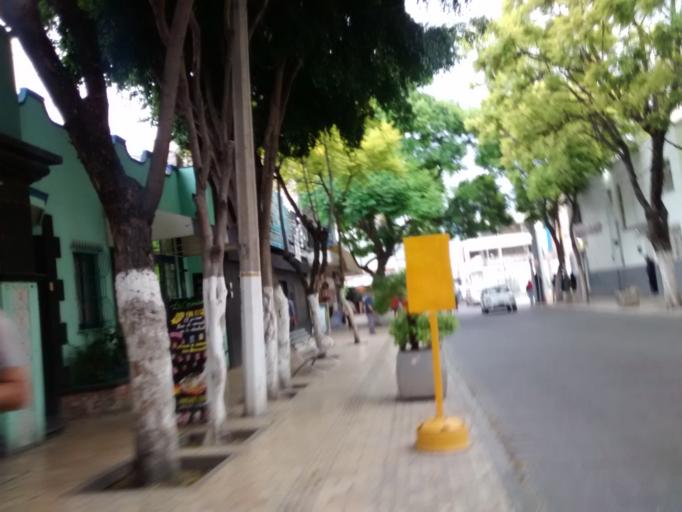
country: MX
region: Puebla
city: Tehuacan
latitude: 18.4654
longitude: -97.3930
